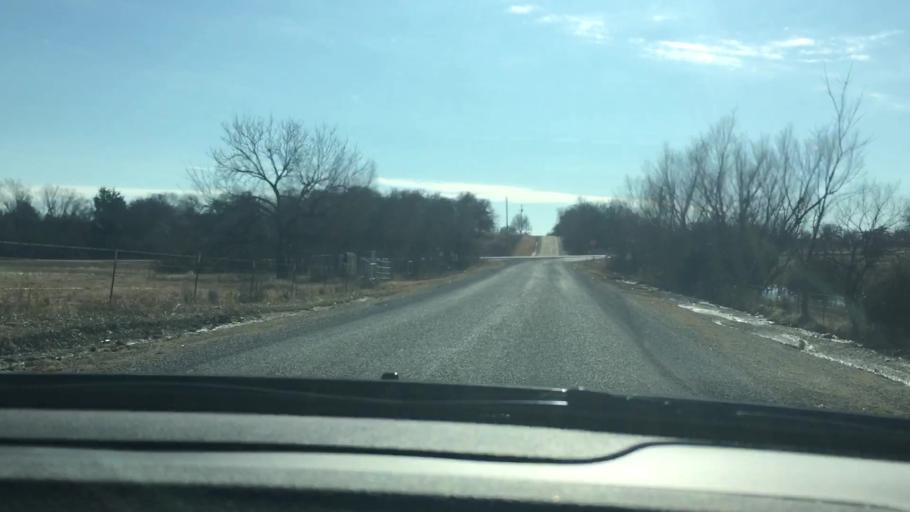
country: US
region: Oklahoma
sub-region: Garvin County
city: Wynnewood
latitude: 34.6527
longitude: -97.0902
